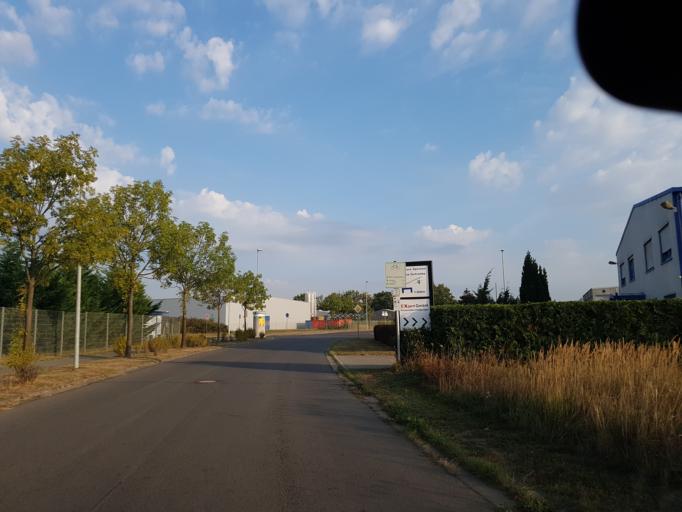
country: DE
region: Brandenburg
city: Elsterwerda
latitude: 51.4603
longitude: 13.5421
